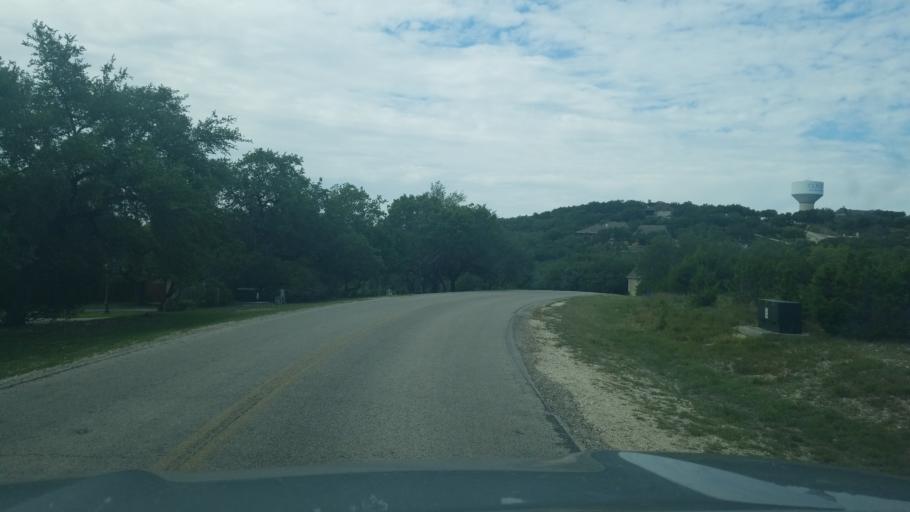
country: US
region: Texas
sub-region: Comal County
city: Bulverde
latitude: 29.8181
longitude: -98.4066
